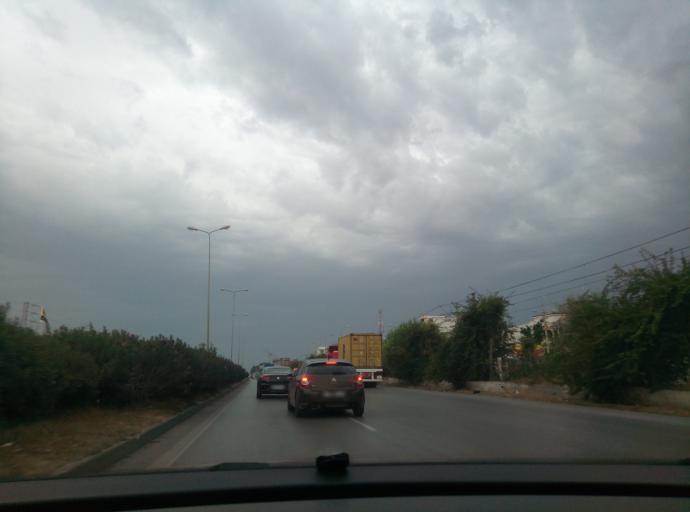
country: TN
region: Bin 'Arus
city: Ben Arous
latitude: 36.7525
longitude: 10.2041
